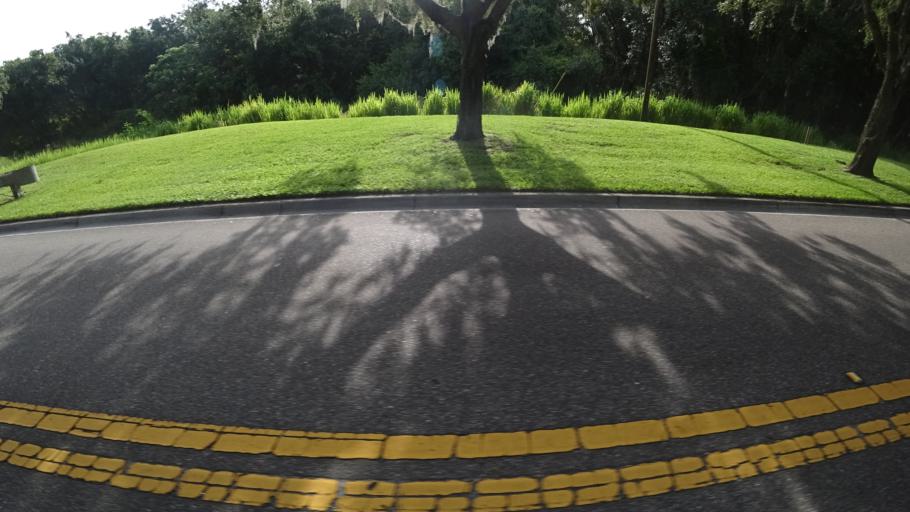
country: US
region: Florida
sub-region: Manatee County
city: Ellenton
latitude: 27.5417
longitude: -82.5034
